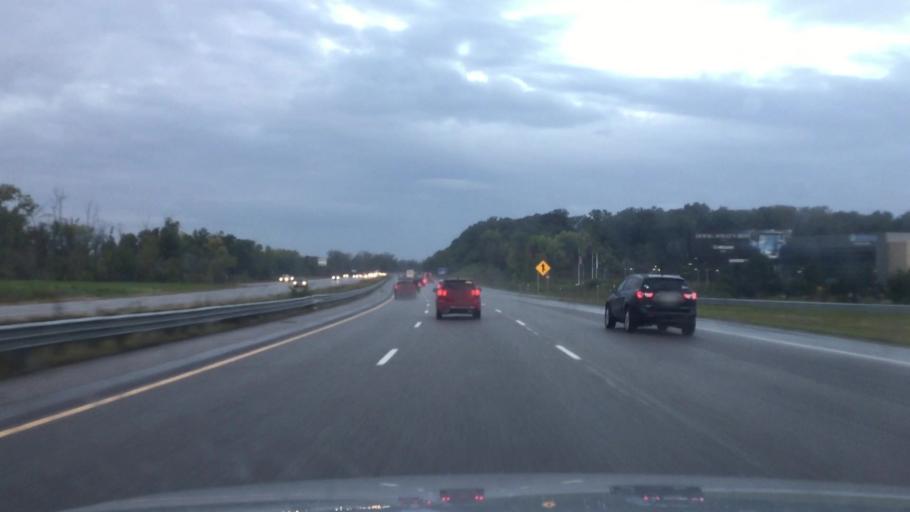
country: US
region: Michigan
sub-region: Genesee County
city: Grand Blanc
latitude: 42.8967
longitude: -83.6350
